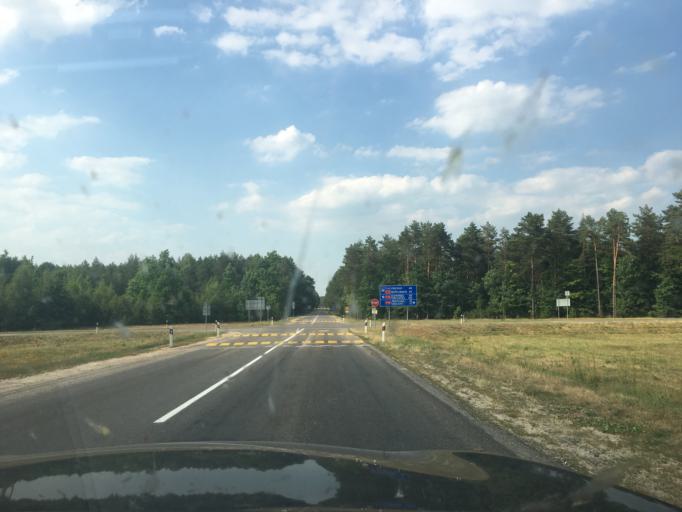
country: BY
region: Brest
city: Pruzhany
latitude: 52.7016
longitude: 24.3081
